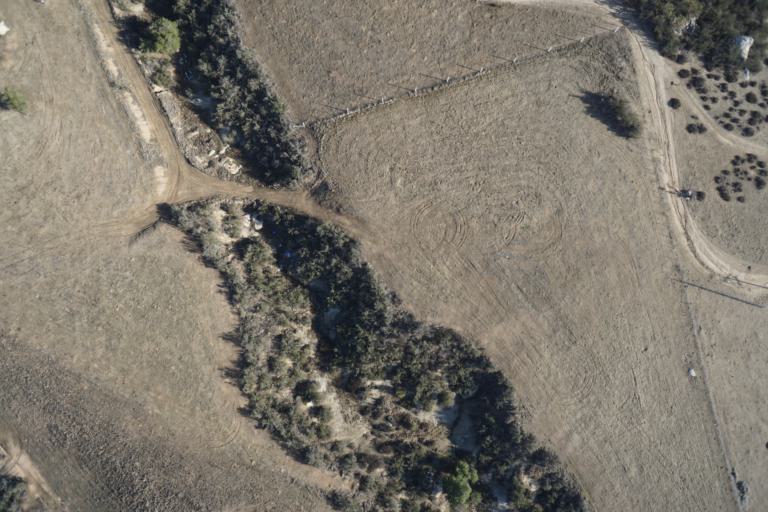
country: US
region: California
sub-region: Riverside County
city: East Hemet
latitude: 33.6250
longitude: -116.8991
